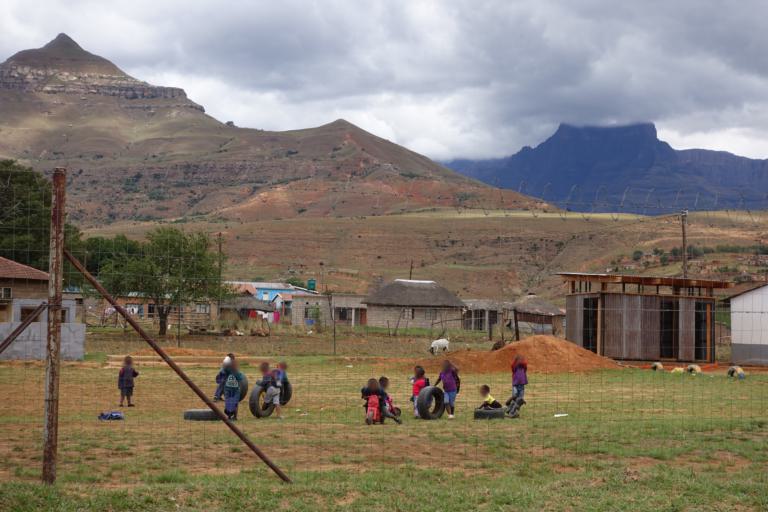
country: ZA
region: Orange Free State
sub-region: Thabo Mofutsanyana District Municipality
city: Phuthaditjhaba
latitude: -28.6850
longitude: 28.9846
